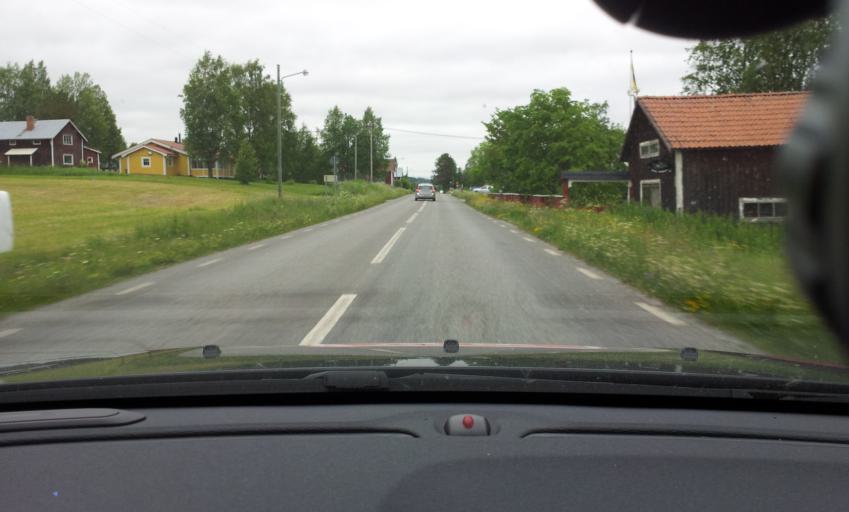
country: SE
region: Jaemtland
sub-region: Krokoms Kommun
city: Krokom
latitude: 63.1600
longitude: 14.1334
